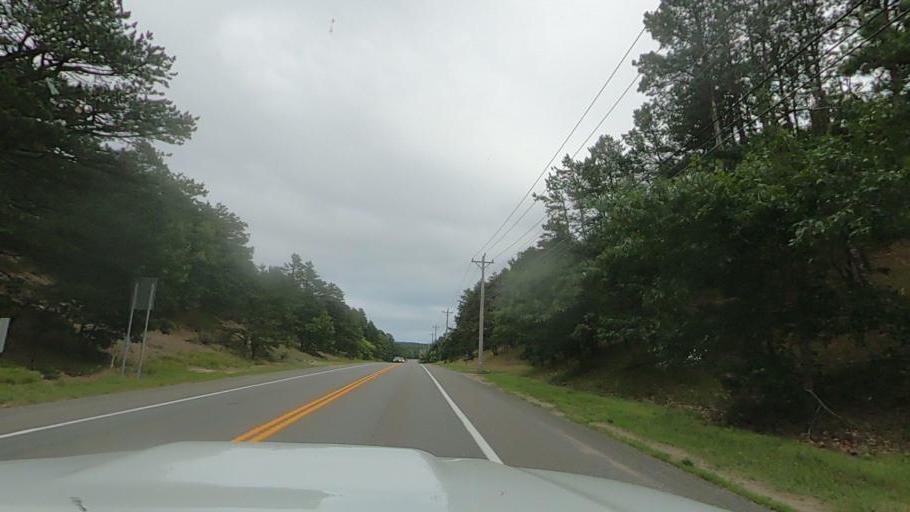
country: US
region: Massachusetts
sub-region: Barnstable County
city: Truro
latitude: 41.9755
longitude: -70.0364
